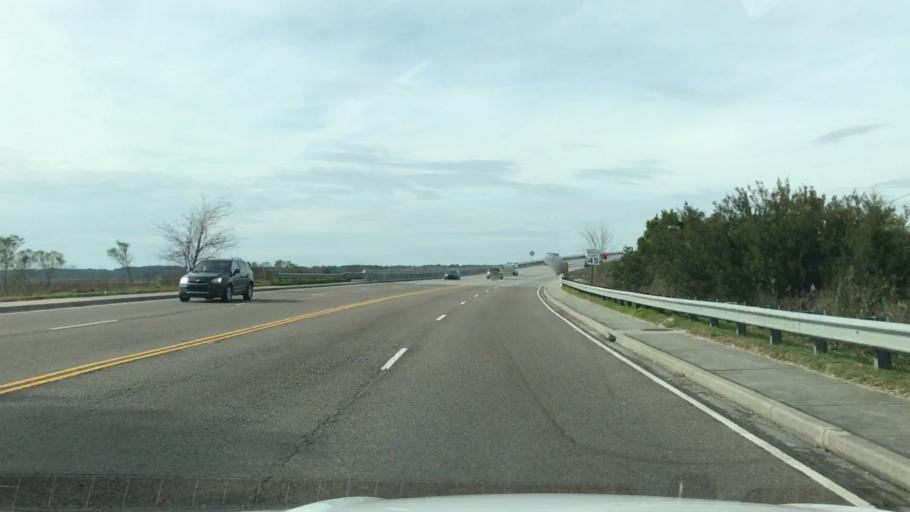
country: US
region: South Carolina
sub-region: Charleston County
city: Charleston
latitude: 32.7539
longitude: -80.0028
